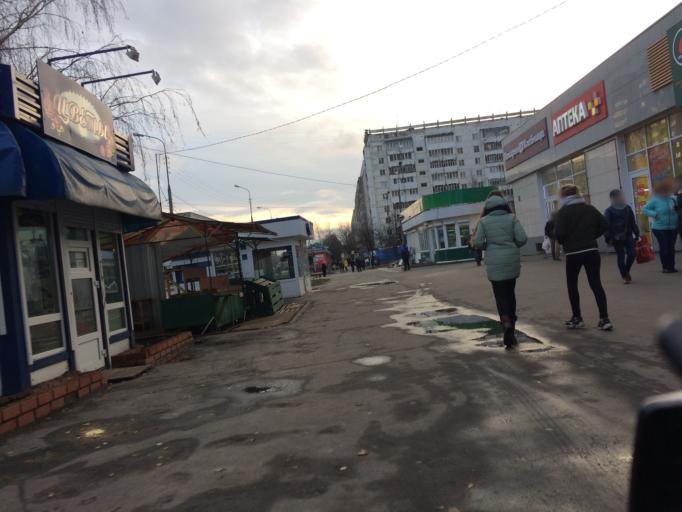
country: RU
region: Mariy-El
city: Yoshkar-Ola
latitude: 56.6315
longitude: 47.9180
